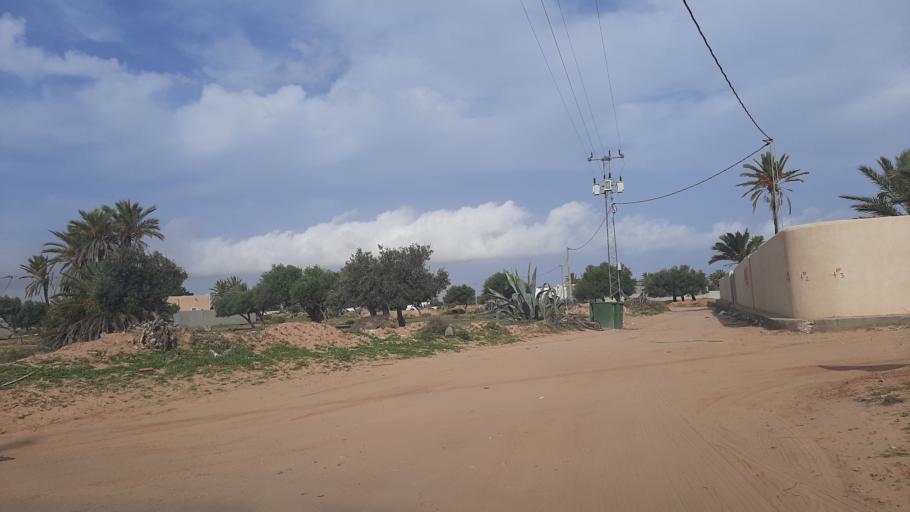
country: TN
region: Madanin
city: Midoun
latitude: 33.8037
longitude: 11.0257
